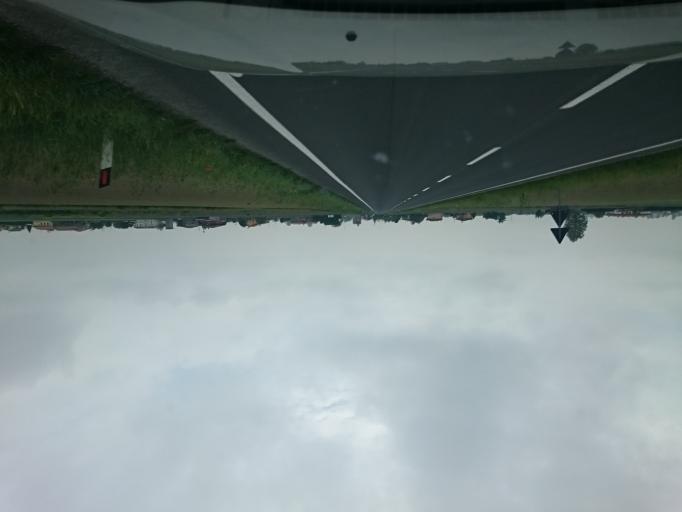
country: IT
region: Veneto
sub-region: Provincia di Padova
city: Codevigo
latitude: 45.2235
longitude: 12.1160
